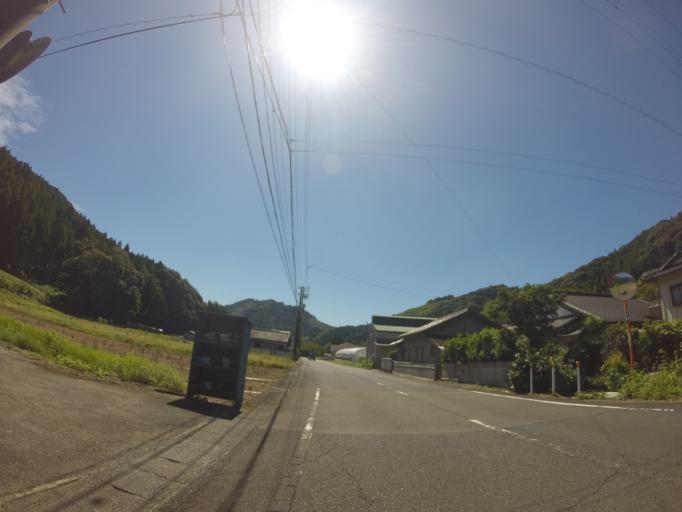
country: JP
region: Shizuoka
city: Fujieda
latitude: 34.9459
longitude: 138.2090
